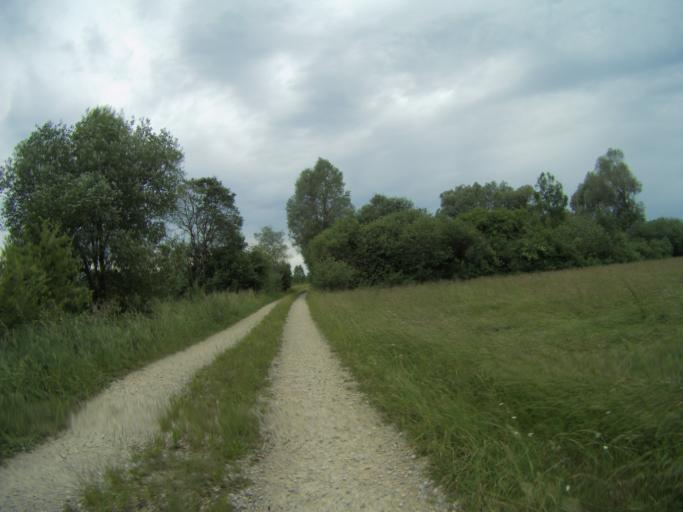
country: DE
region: Bavaria
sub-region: Upper Bavaria
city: Langenbach
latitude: 48.4031
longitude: 11.8785
